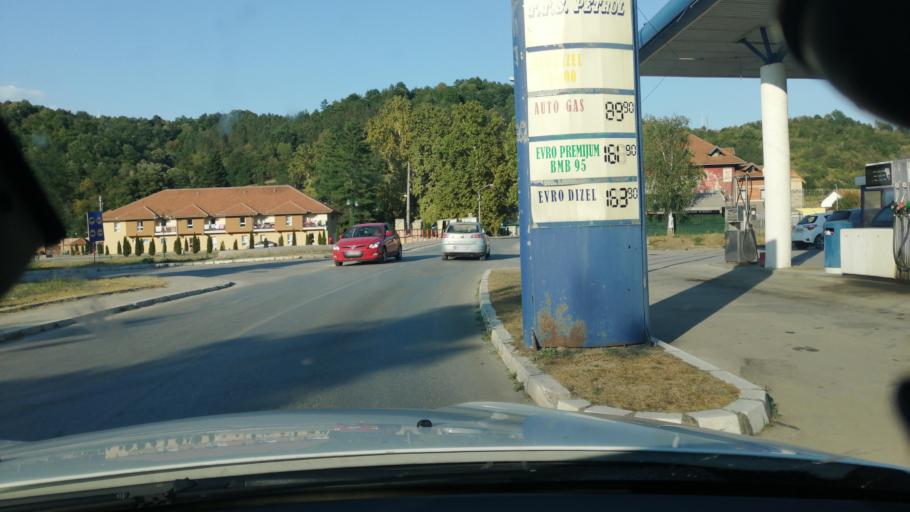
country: RS
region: Central Serbia
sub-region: Moravicki Okrug
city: Lucani
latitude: 43.7740
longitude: 20.2308
